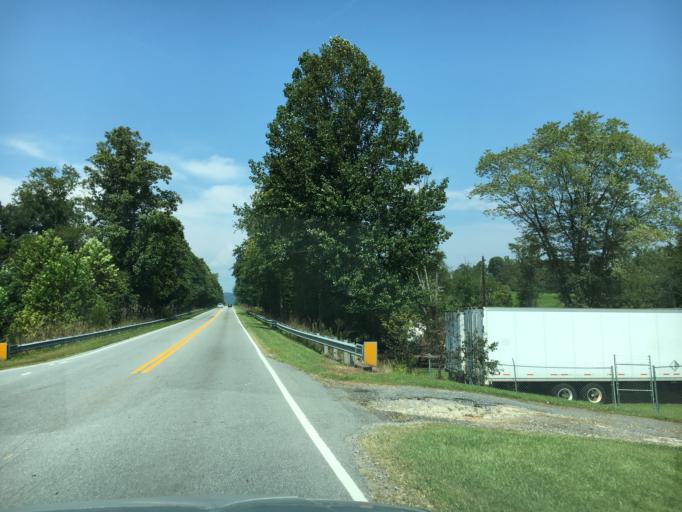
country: US
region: North Carolina
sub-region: McDowell County
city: West Marion
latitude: 35.5964
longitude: -81.9838
